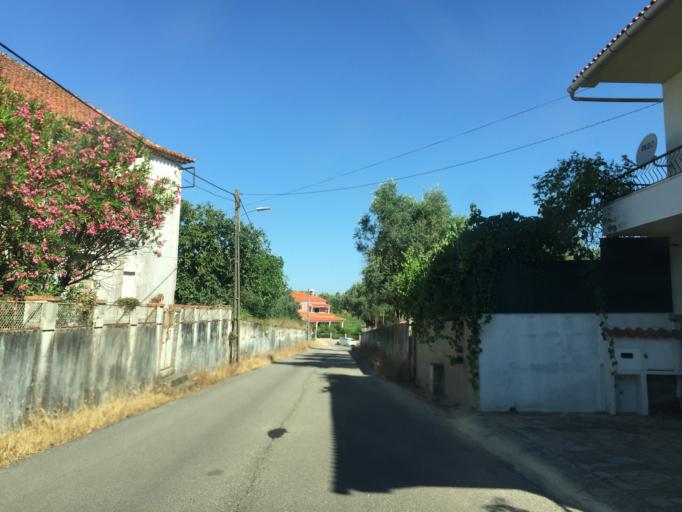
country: PT
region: Santarem
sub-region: Tomar
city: Tomar
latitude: 39.6052
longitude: -8.3298
